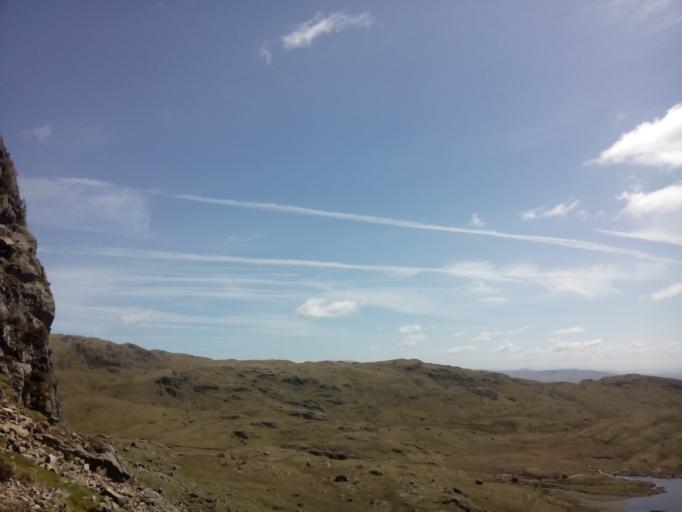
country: GB
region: England
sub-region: Cumbria
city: Keswick
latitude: 54.4619
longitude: -3.1036
